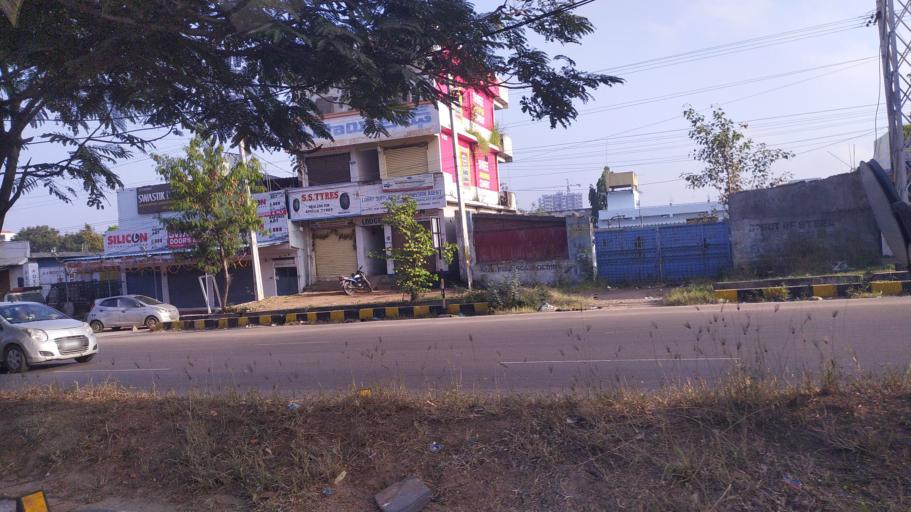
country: IN
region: Telangana
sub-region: Rangareddi
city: Balapur
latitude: 17.3191
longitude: 78.4355
